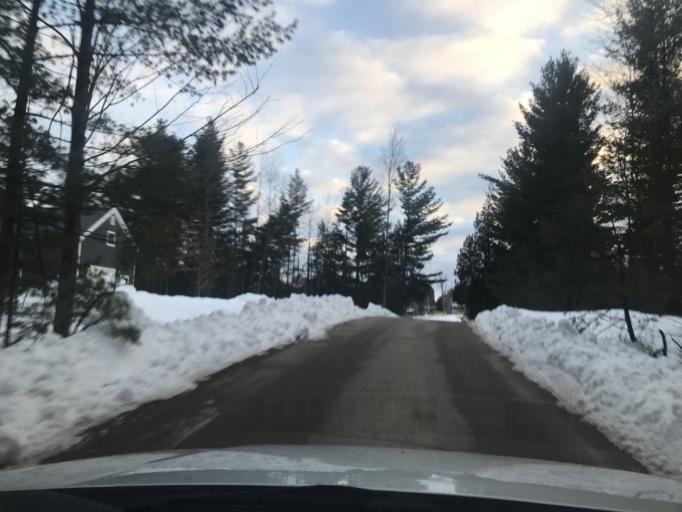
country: US
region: Wisconsin
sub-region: Marinette County
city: Marinette
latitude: 45.1142
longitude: -87.6707
